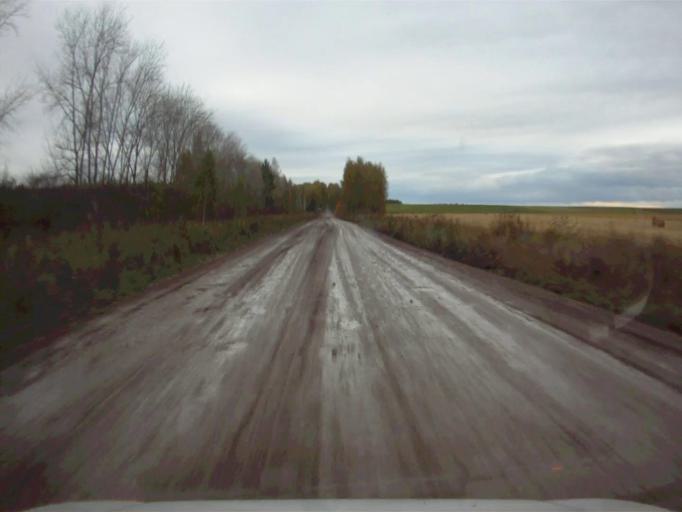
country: RU
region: Sverdlovsk
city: Mikhaylovsk
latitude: 56.1669
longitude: 59.2326
